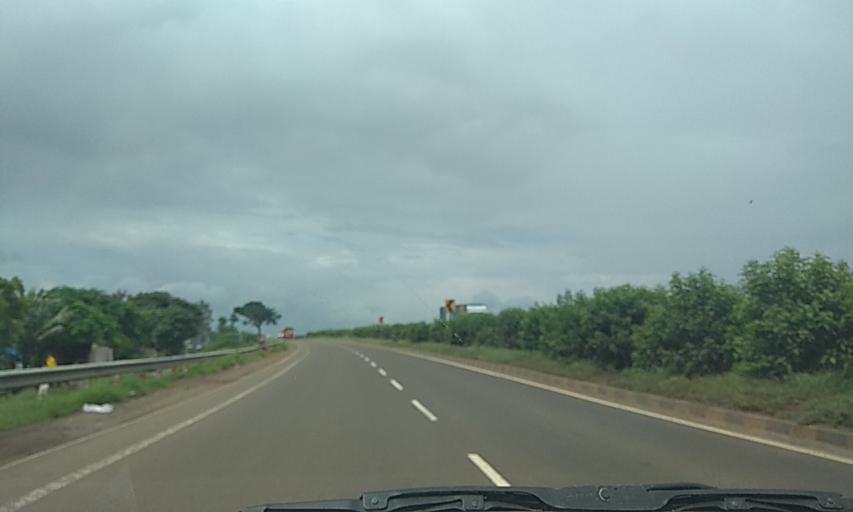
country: IN
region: Maharashtra
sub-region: Kolhapur
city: Kolhapur
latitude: 16.6997
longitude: 74.2777
